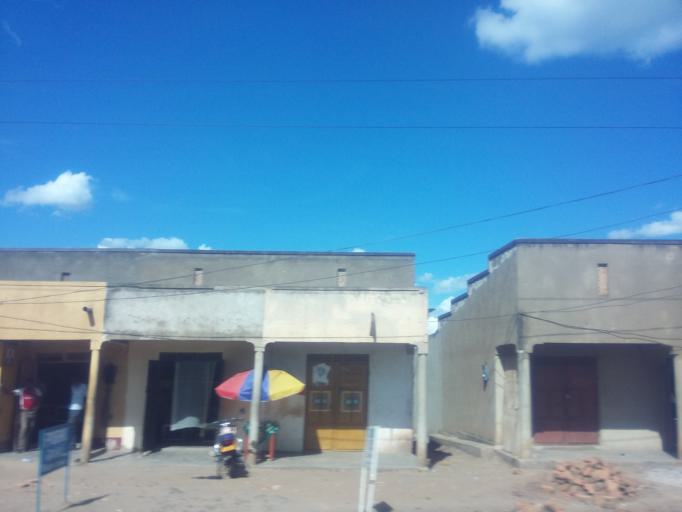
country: UG
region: Western Region
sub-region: Ntungamo District
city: Ntungamo
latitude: -0.9644
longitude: 30.2048
